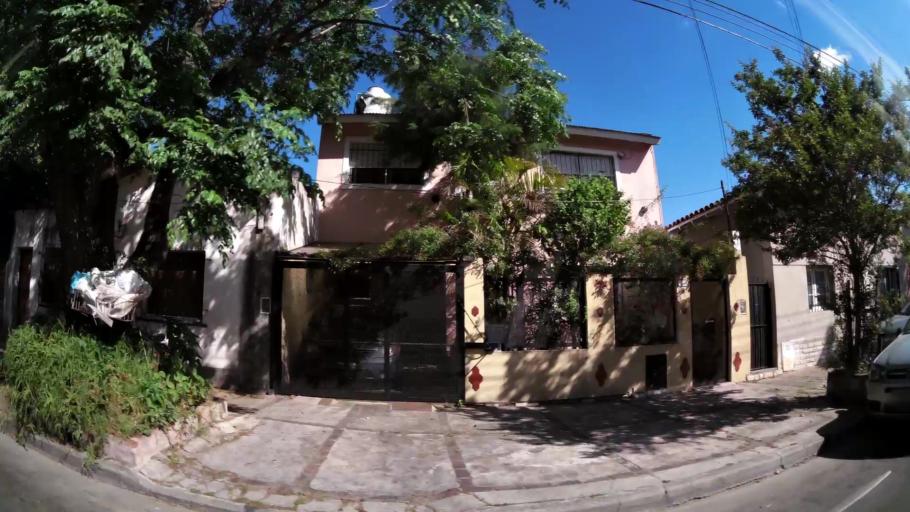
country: AR
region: Buenos Aires
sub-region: Partido de San Isidro
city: San Isidro
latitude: -34.4626
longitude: -58.5351
